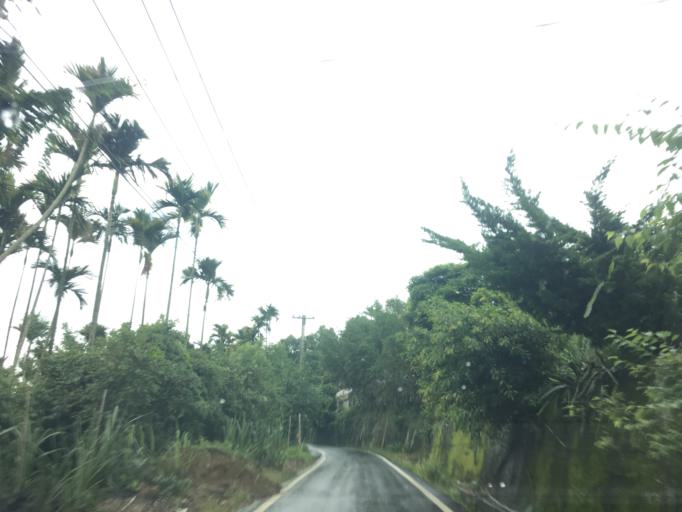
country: TW
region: Taiwan
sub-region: Yunlin
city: Douliu
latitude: 23.5603
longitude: 120.6562
